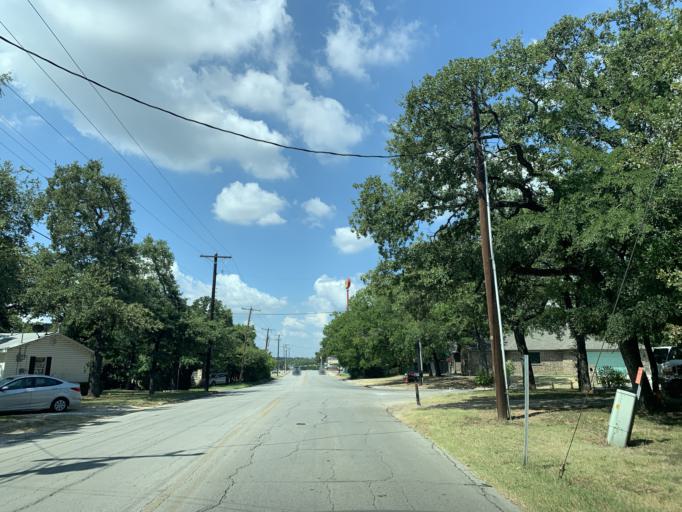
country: US
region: Texas
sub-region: Tarrant County
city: Azle
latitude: 32.8934
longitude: -97.5366
